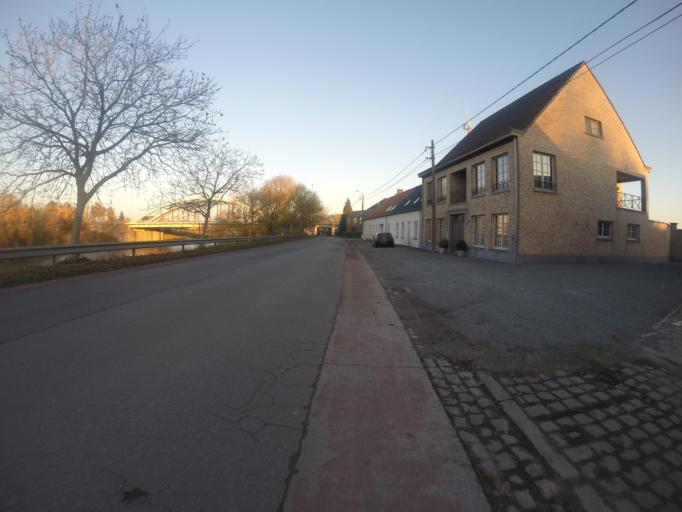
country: BE
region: Flanders
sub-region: Provincie Oost-Vlaanderen
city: Aalter
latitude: 51.1065
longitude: 3.4333
